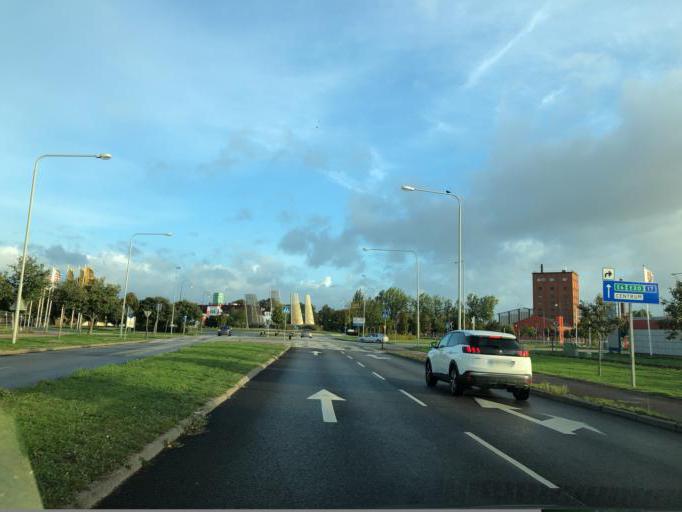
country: SE
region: Skane
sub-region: Landskrona
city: Landskrona
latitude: 55.8702
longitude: 12.8509
